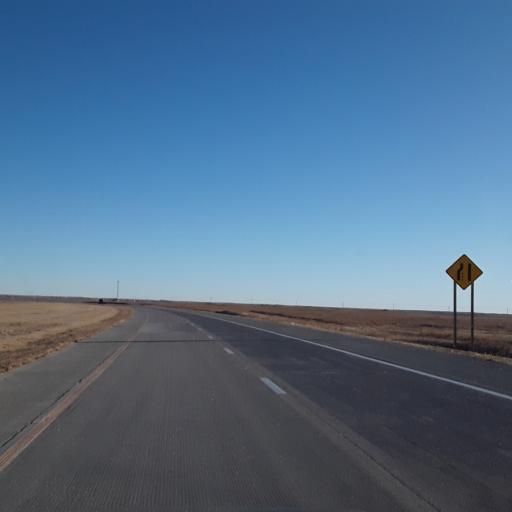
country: US
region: Kansas
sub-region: Seward County
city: Liberal
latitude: 37.1125
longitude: -100.7783
